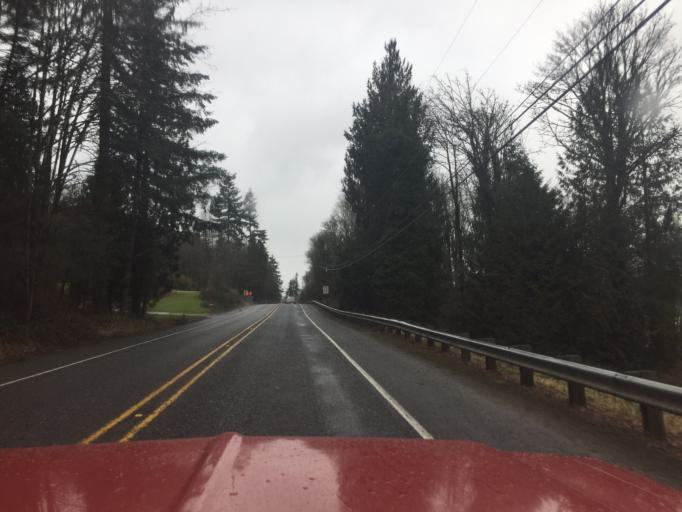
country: US
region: Oregon
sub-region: Columbia County
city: Rainier
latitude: 46.0793
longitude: -122.9109
